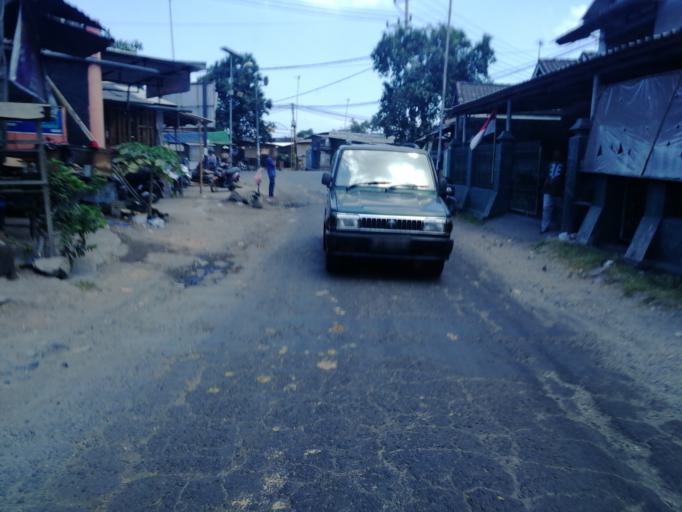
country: ID
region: West Nusa Tenggara
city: Jelateng Timur
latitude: -8.7264
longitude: 116.0758
